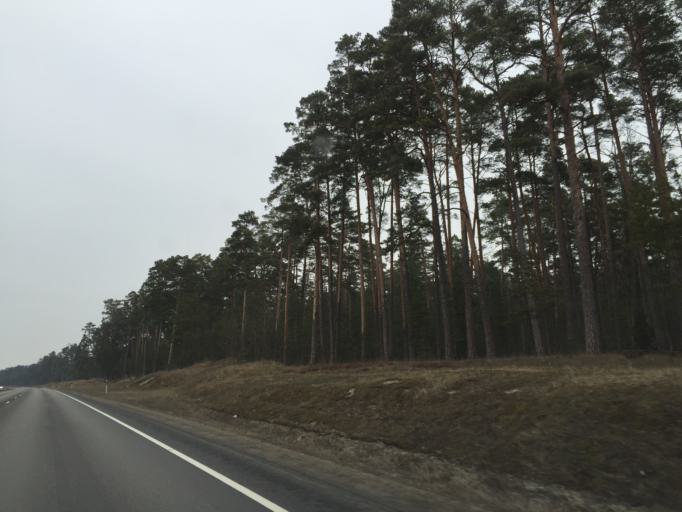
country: EE
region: Paernumaa
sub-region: Paernu linn
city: Parnu
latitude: 58.1861
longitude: 24.4920
